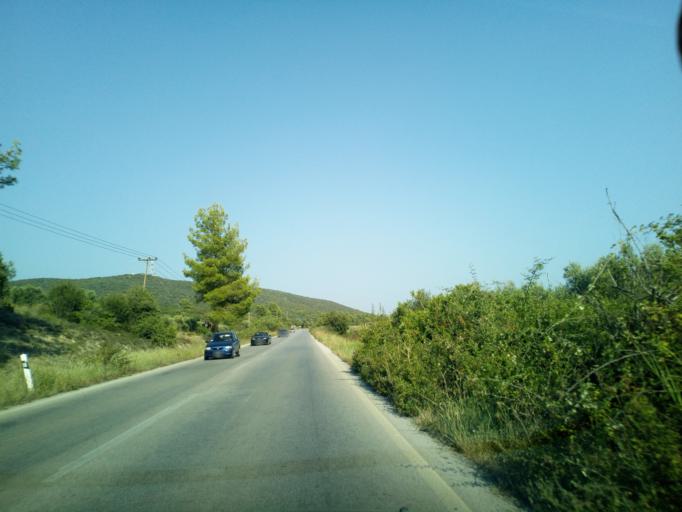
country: GR
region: Central Macedonia
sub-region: Nomos Chalkidikis
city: Ormylia
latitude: 40.2511
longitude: 23.5688
